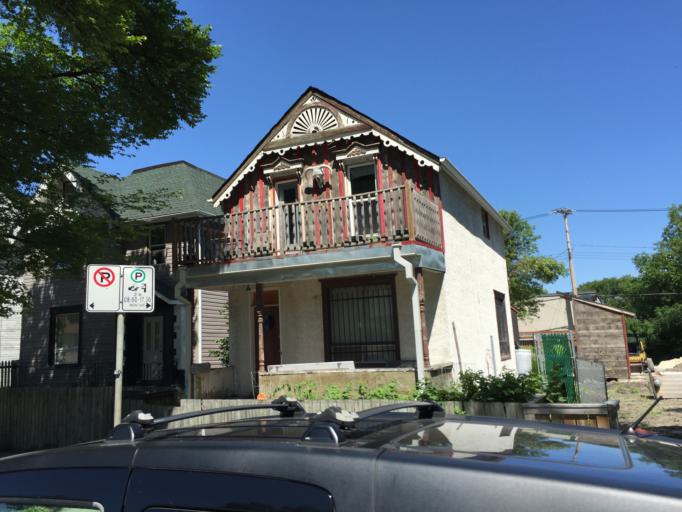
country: CA
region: Manitoba
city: Winnipeg
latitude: 49.9017
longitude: -97.1442
